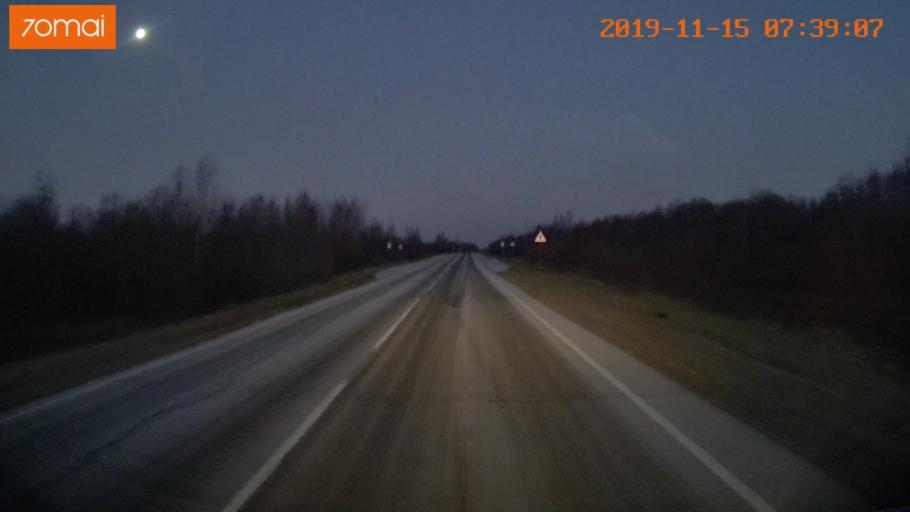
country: RU
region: Vologda
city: Sheksna
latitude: 58.7625
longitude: 38.3902
